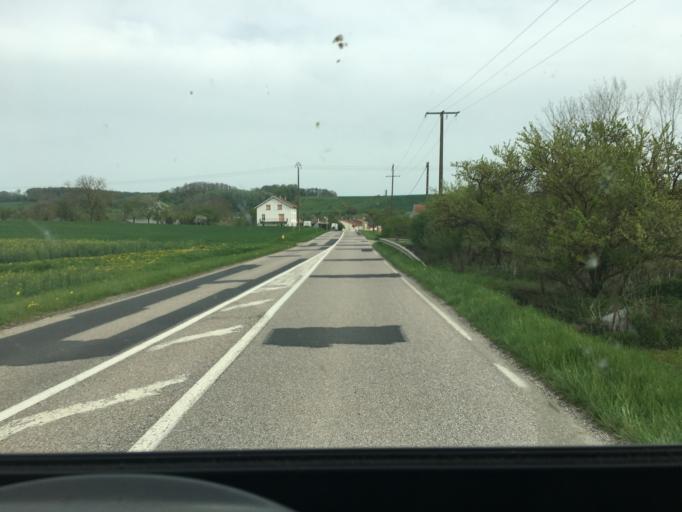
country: FR
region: Lorraine
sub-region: Departement de Meurthe-et-Moselle
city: Einville-au-Jard
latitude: 48.6758
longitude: 6.4907
